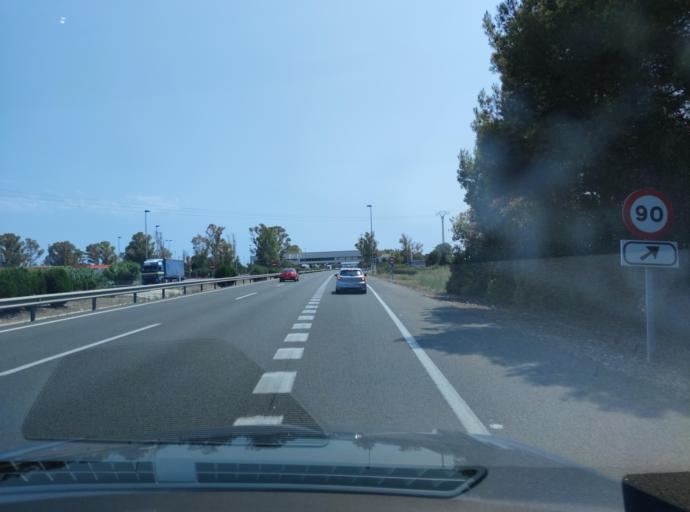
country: ES
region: Valencia
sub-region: Provincia de Castello
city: Alquerias del Nino Perdido
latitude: 39.8679
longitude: -0.1223
